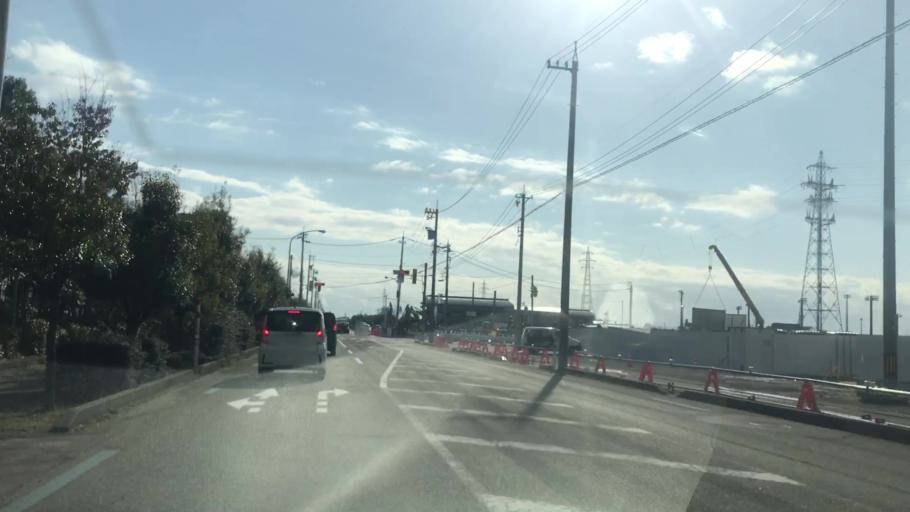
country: JP
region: Toyama
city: Takaoka
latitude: 36.7242
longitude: 137.0146
